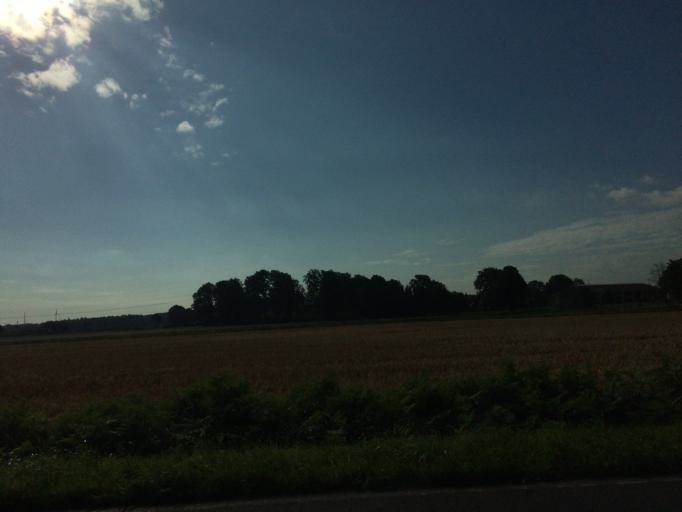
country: DE
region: North Rhine-Westphalia
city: Dorsten
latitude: 51.6855
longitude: 6.9912
